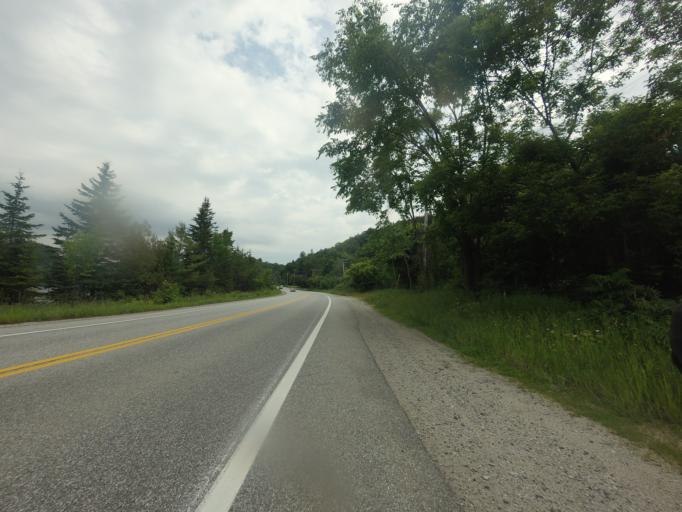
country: CA
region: Quebec
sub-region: Outaouais
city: Wakefield
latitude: 45.6899
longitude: -75.9320
